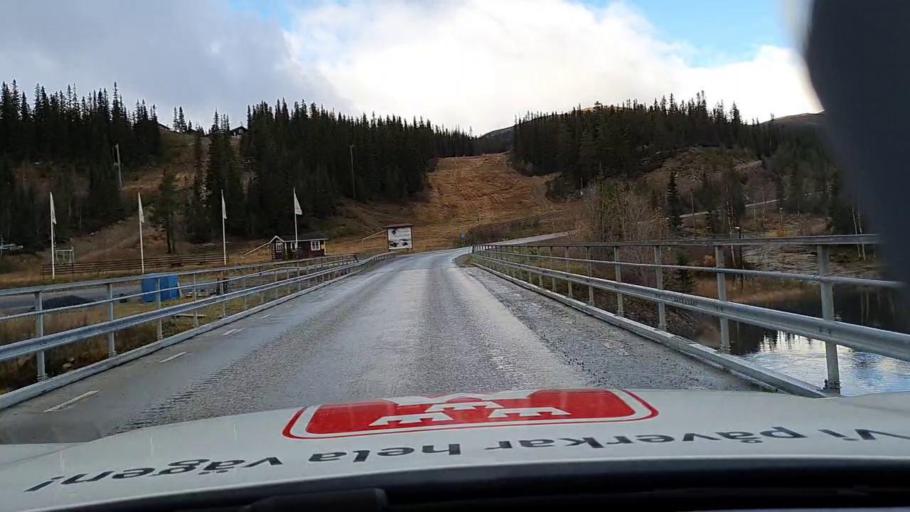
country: SE
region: Jaemtland
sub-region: Are Kommun
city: Jarpen
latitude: 63.0864
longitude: 13.7724
